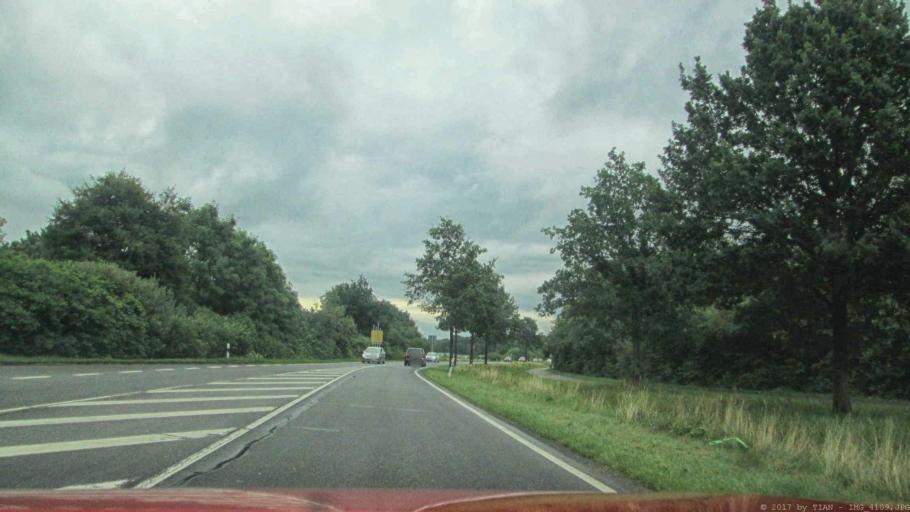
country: DE
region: Lower Saxony
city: Wolfsburg
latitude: 52.4271
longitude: 10.8258
